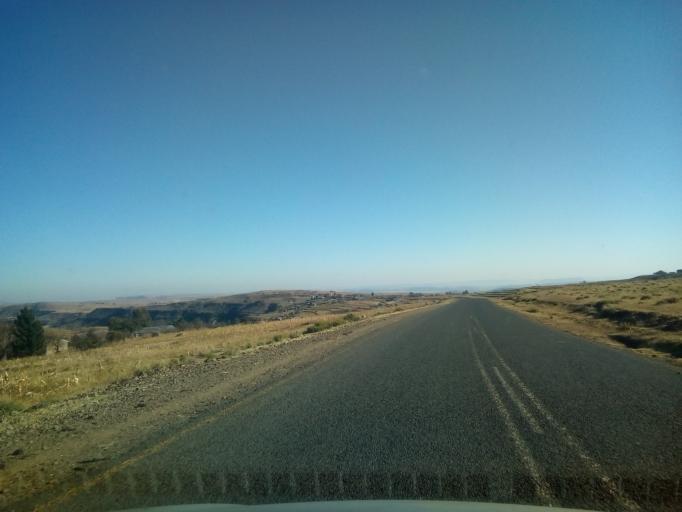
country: LS
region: Berea
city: Teyateyaneng
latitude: -29.2613
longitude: 27.8056
